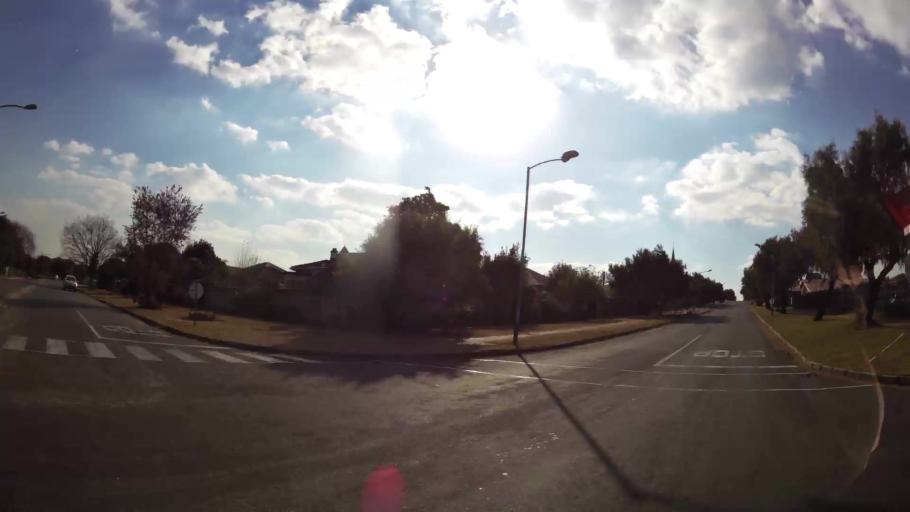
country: ZA
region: Gauteng
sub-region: West Rand District Municipality
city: Krugersdorp
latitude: -26.0893
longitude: 27.7708
